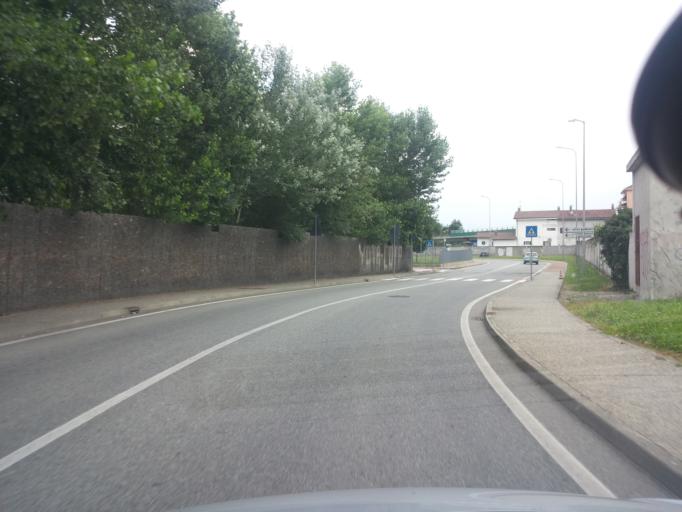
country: IT
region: Piedmont
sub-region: Provincia di Torino
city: Ivrea
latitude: 45.4586
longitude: 7.8800
